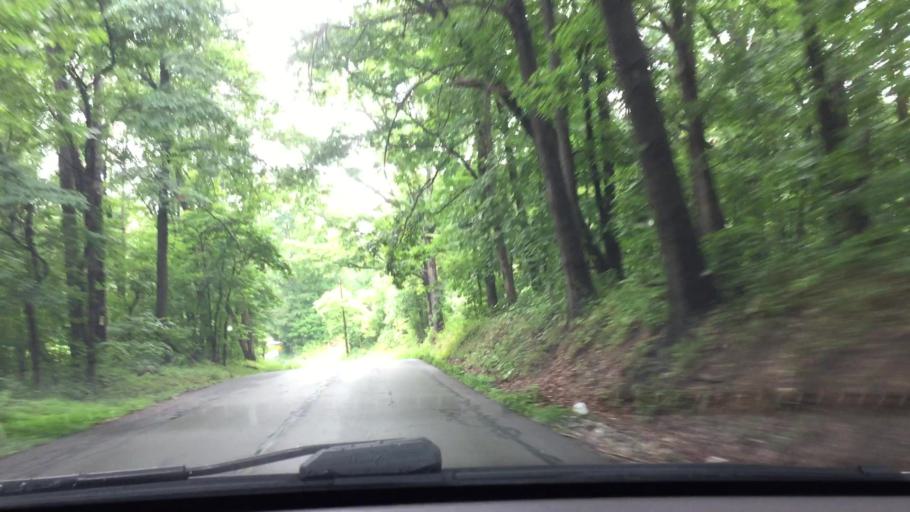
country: US
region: Pennsylvania
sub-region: Washington County
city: Cecil-Bishop
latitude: 40.3075
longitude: -80.1988
